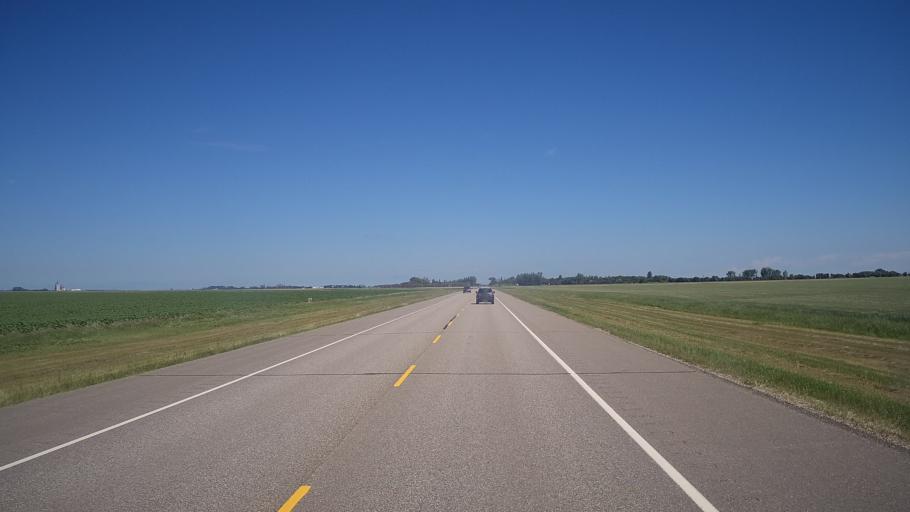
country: CA
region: Manitoba
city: Portage la Prairie
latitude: 50.0421
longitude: -98.4687
